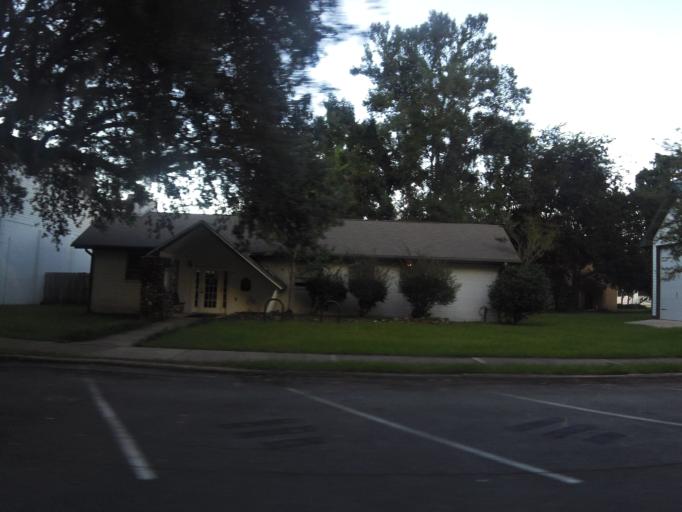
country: US
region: Georgia
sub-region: Camden County
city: St. Marys
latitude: 30.7253
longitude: -81.5474
